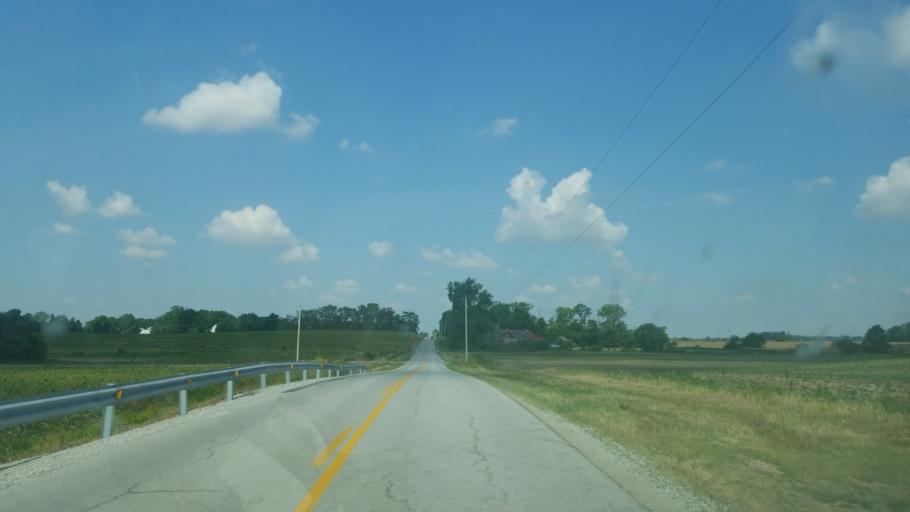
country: US
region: Ohio
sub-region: Auglaize County
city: Wapakoneta
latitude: 40.5709
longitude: -84.0941
